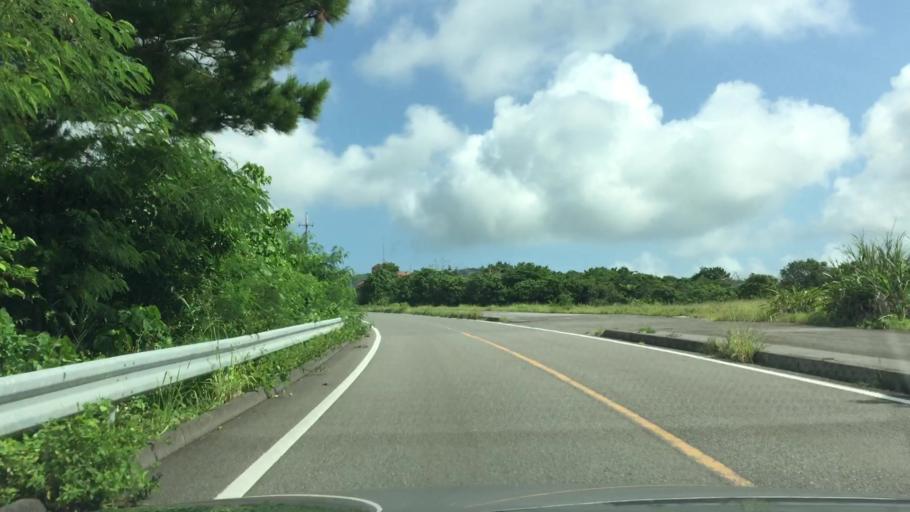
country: JP
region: Okinawa
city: Ishigaki
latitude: 24.4184
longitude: 124.2150
